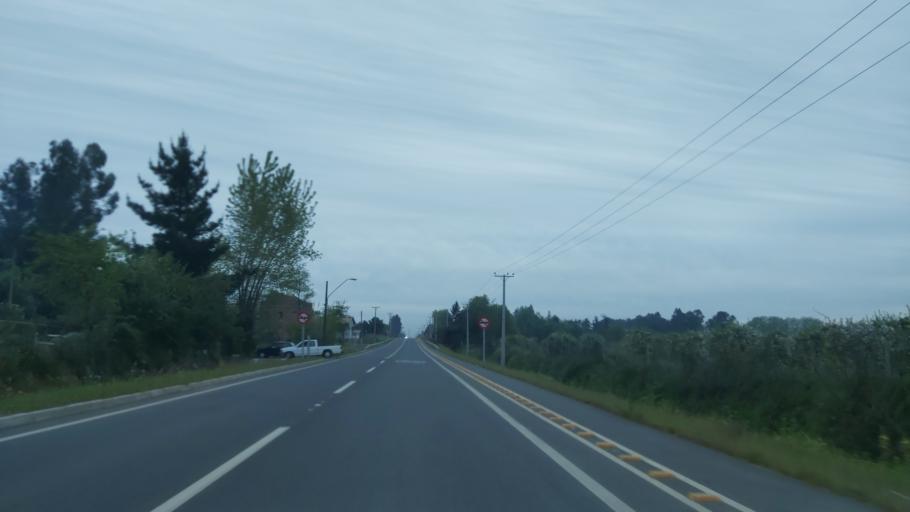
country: CL
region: Maule
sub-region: Provincia de Linares
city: Colbun
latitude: -35.6856
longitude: -71.4766
